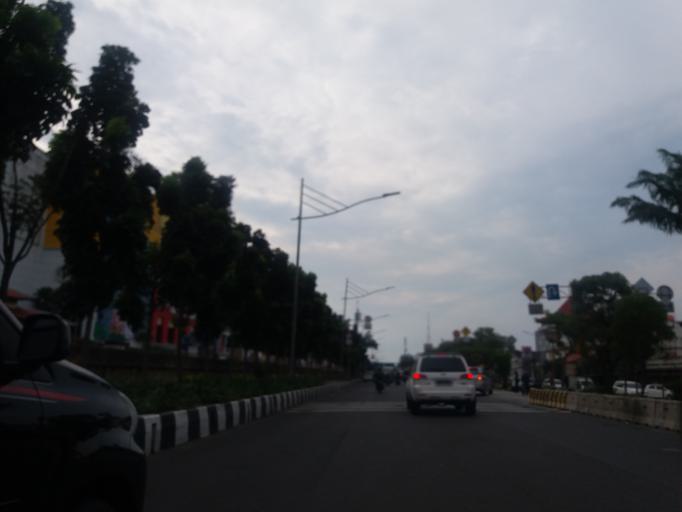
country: ID
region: Jakarta Raya
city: Jakarta
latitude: -6.1403
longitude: 106.8330
